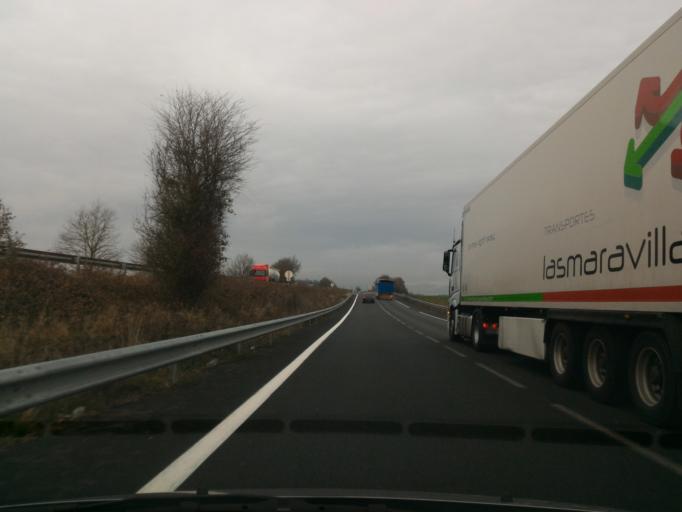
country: FR
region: Poitou-Charentes
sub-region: Departement de la Vienne
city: Iteuil
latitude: 46.4798
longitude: 0.2712
